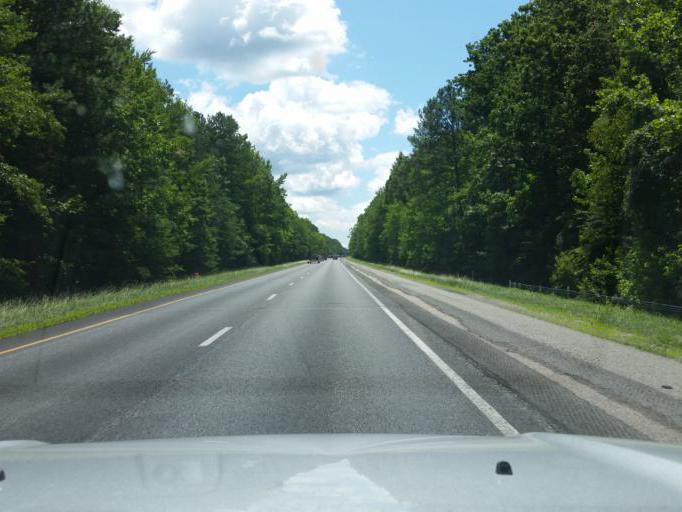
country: US
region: Virginia
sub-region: New Kent County
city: New Kent
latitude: 37.4669
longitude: -76.8953
